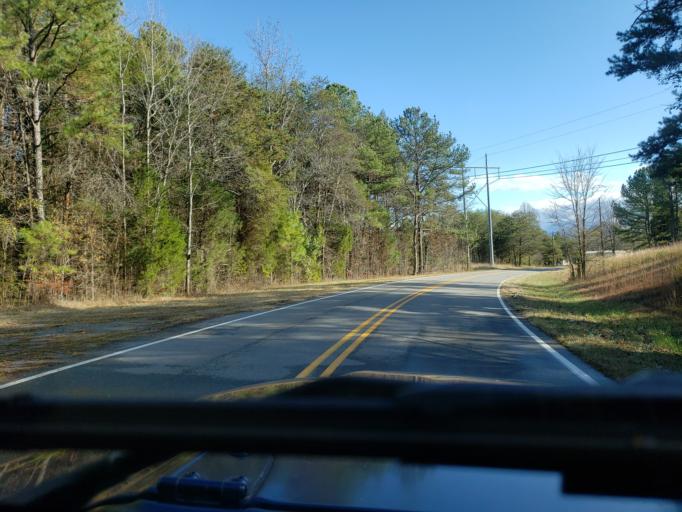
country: US
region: North Carolina
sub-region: Cleveland County
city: White Plains
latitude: 35.1683
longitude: -81.4285
